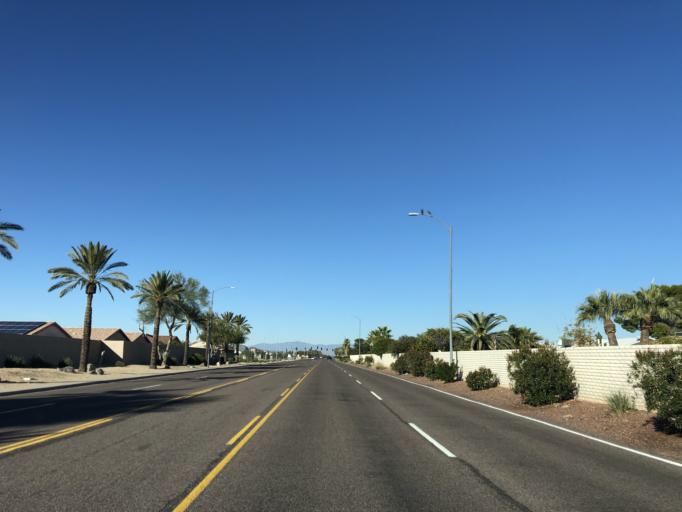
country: US
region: Arizona
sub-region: Maricopa County
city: Sun City West
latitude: 33.6641
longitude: -112.2899
